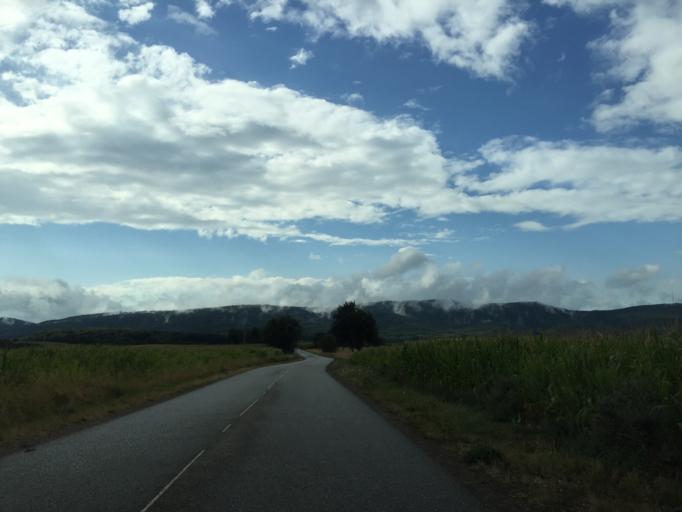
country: FR
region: Alsace
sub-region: Departement du Bas-Rhin
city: Soultz-sous-Forets
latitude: 48.9801
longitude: 7.9064
